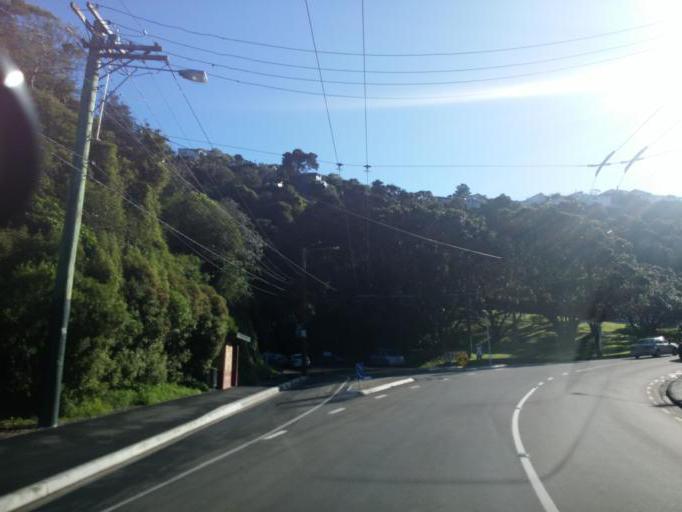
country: NZ
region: Wellington
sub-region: Wellington City
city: Kelburn
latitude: -41.2938
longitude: 174.7613
